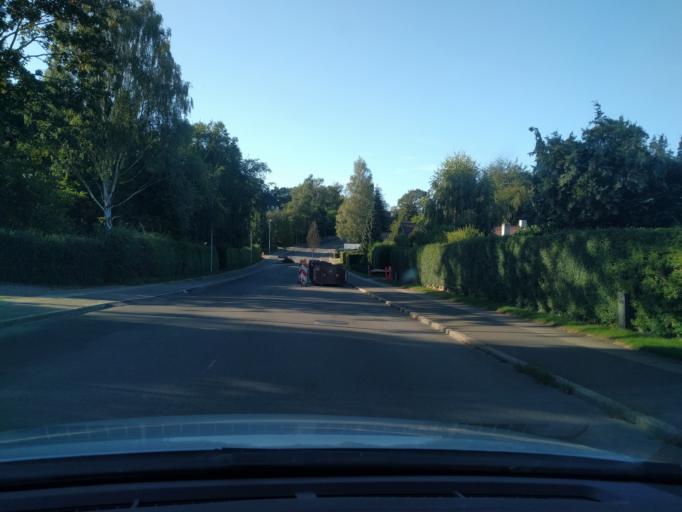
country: DK
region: Central Jutland
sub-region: Horsens Kommune
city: Horsens
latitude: 55.8681
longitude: 9.8996
